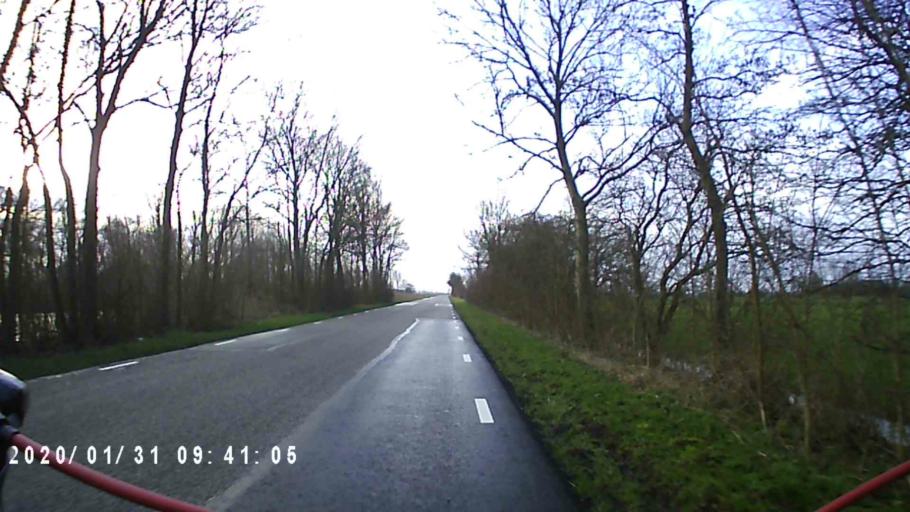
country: NL
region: Groningen
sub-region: Gemeente Zuidhorn
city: Aduard
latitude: 53.2832
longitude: 6.4844
